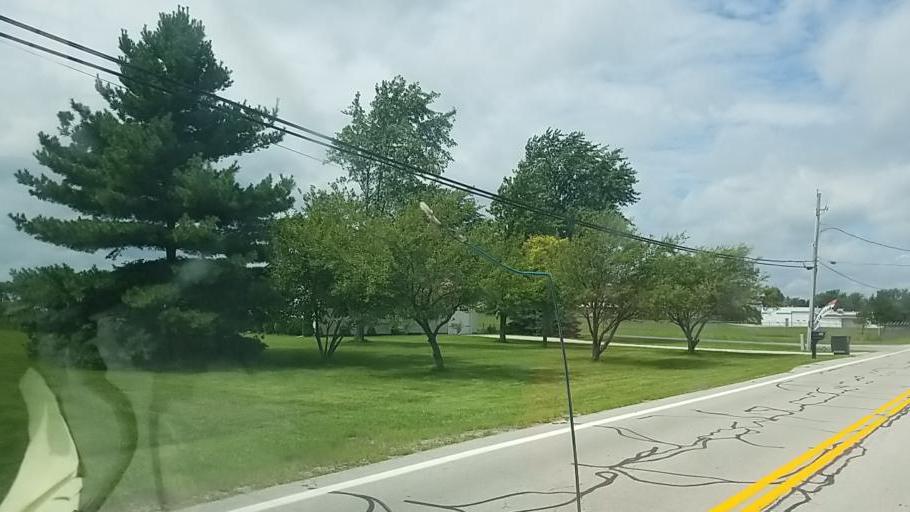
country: US
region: Ohio
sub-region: Fayette County
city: Jeffersonville
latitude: 39.6609
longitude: -83.5711
